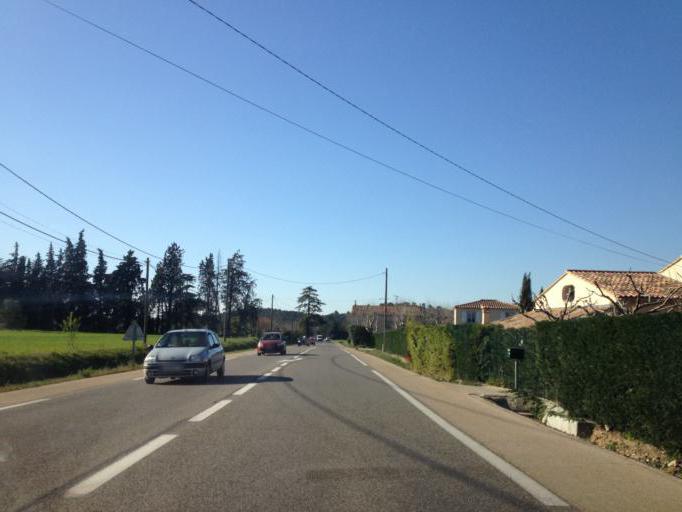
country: FR
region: Provence-Alpes-Cote d'Azur
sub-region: Departement des Bouches-du-Rhone
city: Bouc-Bel-Air
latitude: 43.5010
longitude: 5.4007
